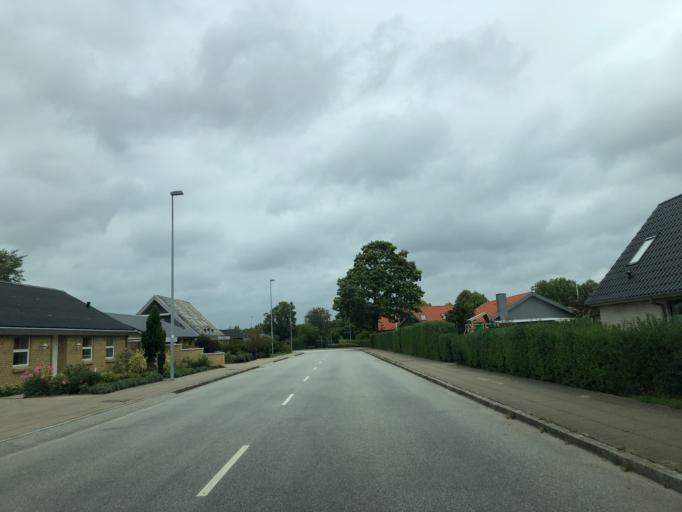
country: DK
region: Central Jutland
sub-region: Herning Kommune
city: Snejbjerg
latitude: 56.1298
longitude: 8.8992
